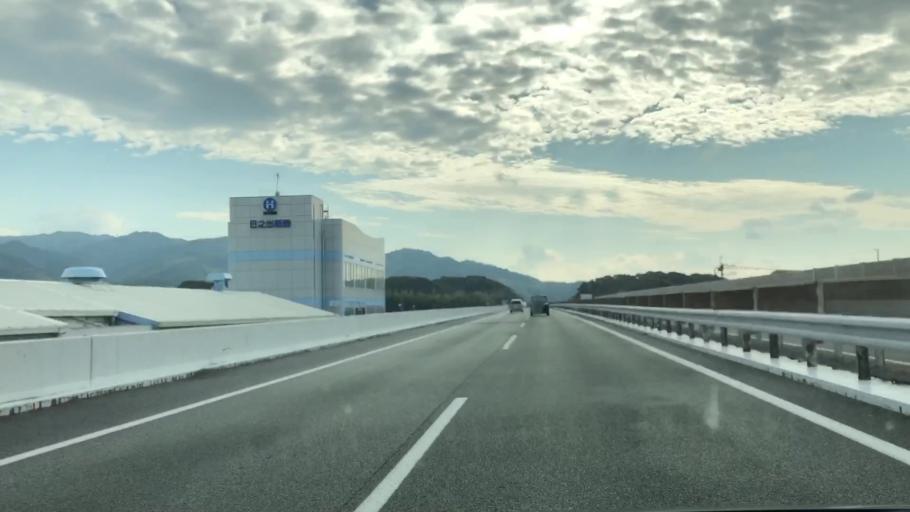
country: JP
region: Fukuoka
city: Setakamachi-takayanagi
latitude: 33.1861
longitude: 130.5190
